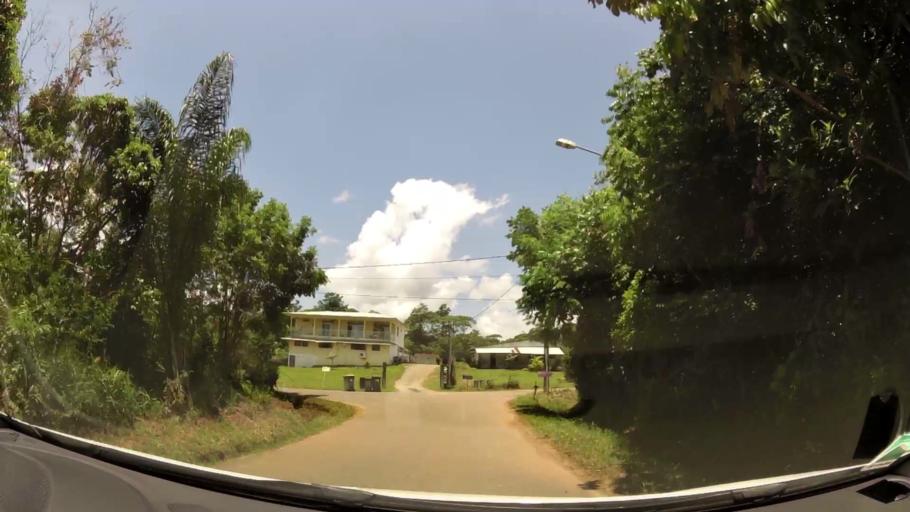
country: GF
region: Guyane
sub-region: Guyane
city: Matoury
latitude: 4.8788
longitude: -52.3398
